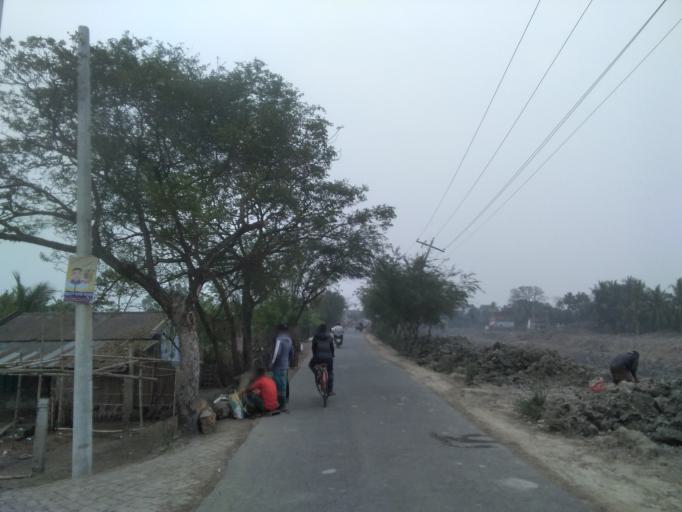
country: BD
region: Khulna
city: Satkhira
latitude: 22.5846
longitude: 89.0666
